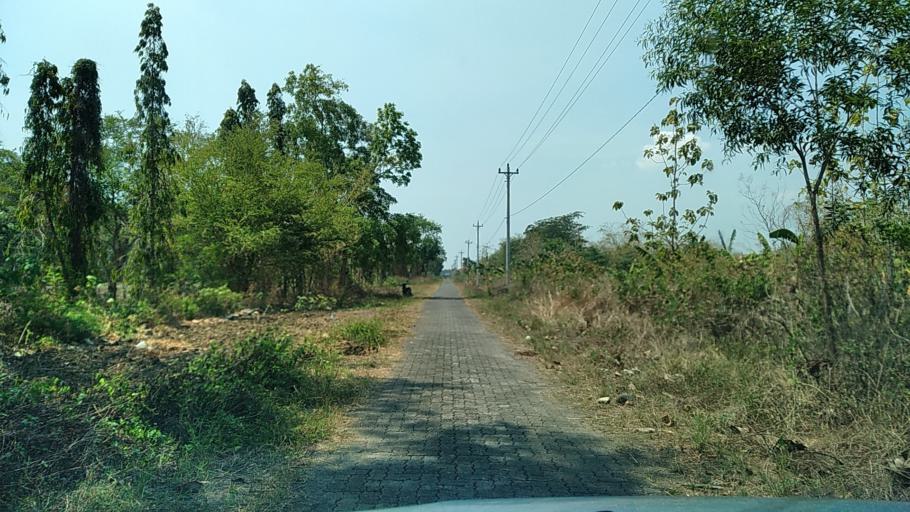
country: ID
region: Central Java
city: Mranggen
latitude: -7.0360
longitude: 110.4805
